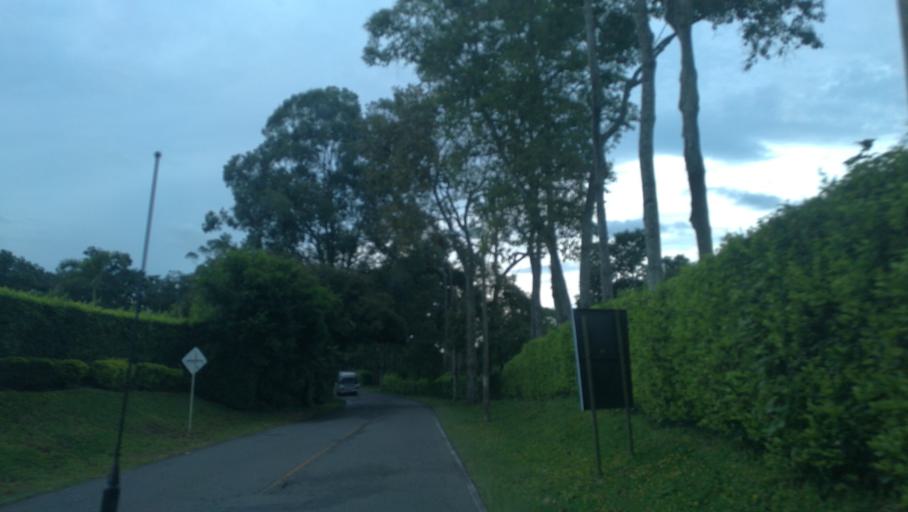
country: CO
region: Quindio
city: Montenegro
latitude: 4.5200
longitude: -75.7813
